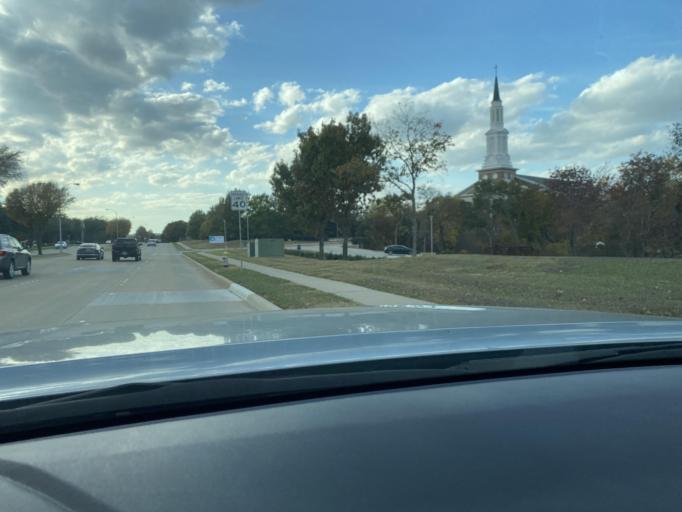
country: US
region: Texas
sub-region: Dallas County
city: Addison
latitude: 33.0168
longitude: -96.8183
